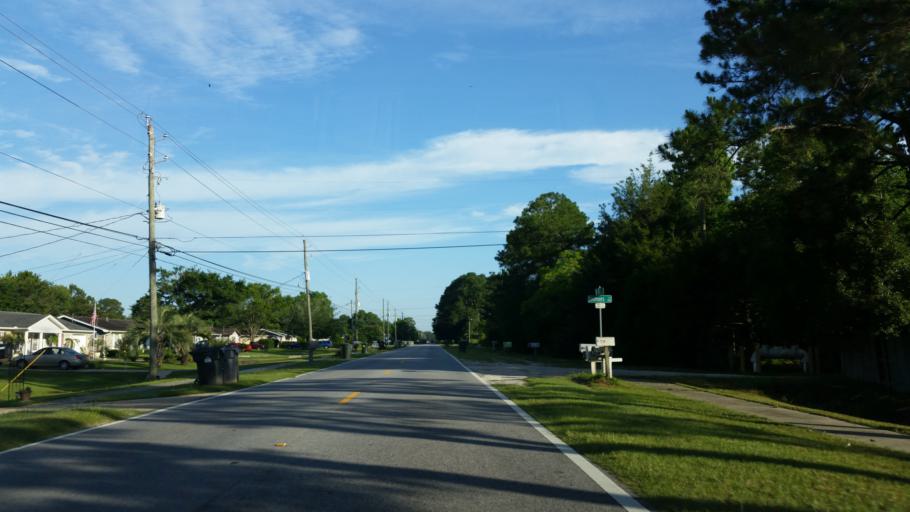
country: US
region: Florida
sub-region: Escambia County
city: Myrtle Grove
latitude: 30.3898
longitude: -87.3612
